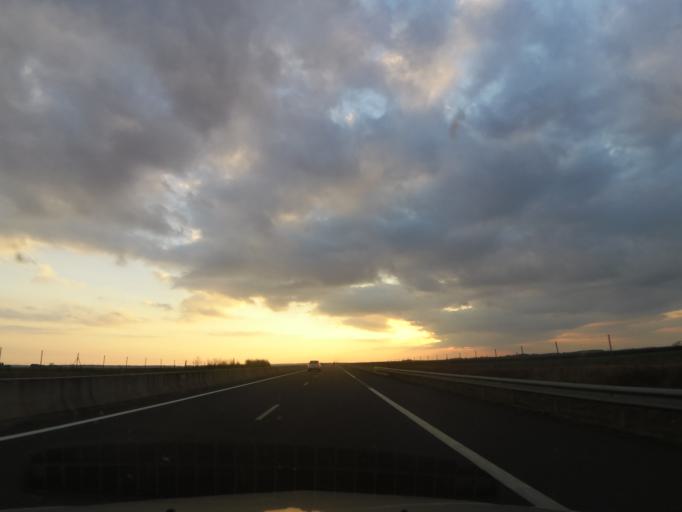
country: FR
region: Centre
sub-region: Departement du Loiret
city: Ascheres-le-Marche
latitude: 48.0639
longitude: 1.9538
